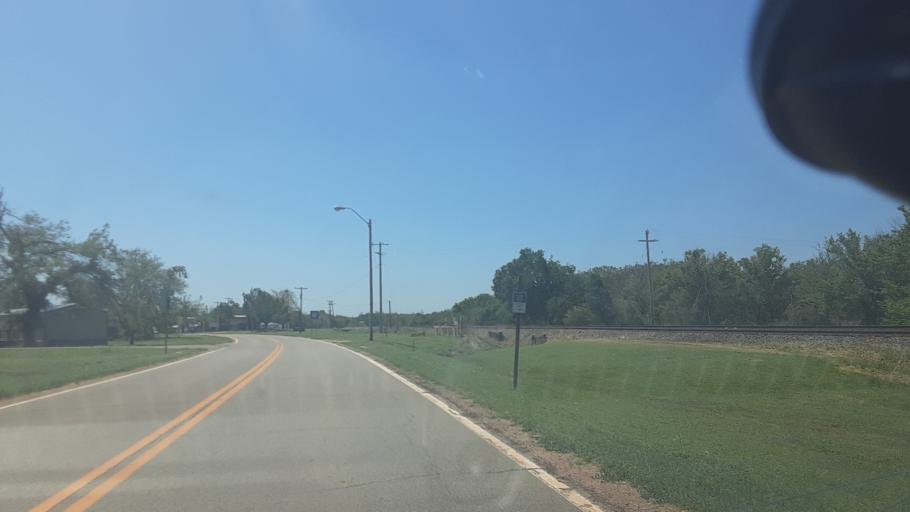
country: US
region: Oklahoma
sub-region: Logan County
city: Guthrie
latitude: 36.0687
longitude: -97.4067
